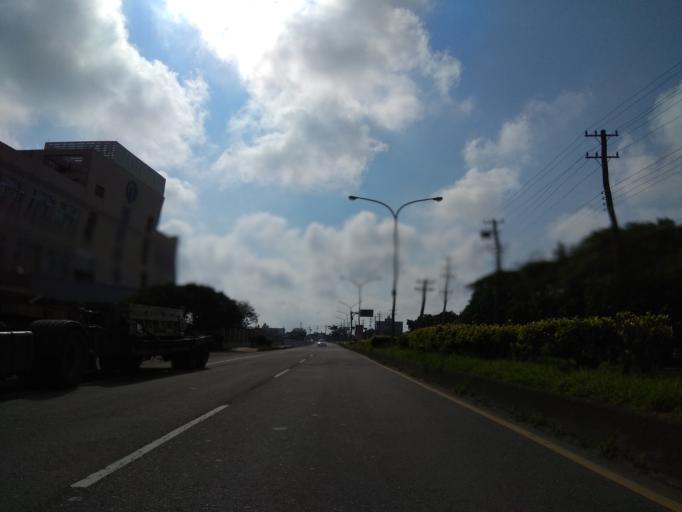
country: TW
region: Taiwan
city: Taoyuan City
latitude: 25.0431
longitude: 121.1062
